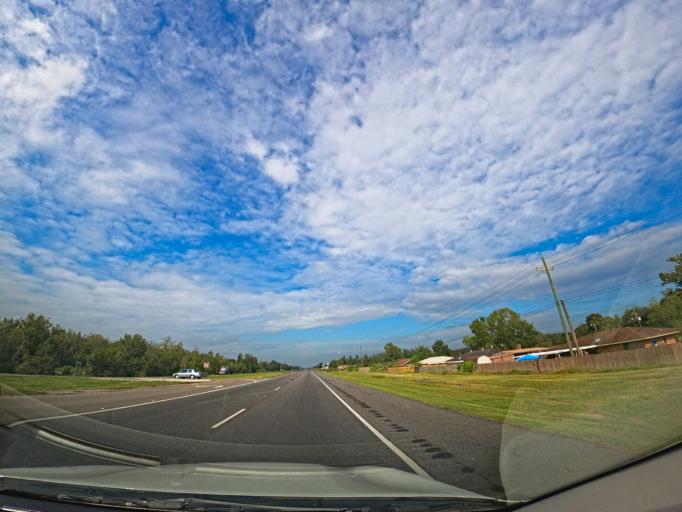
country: US
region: Louisiana
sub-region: Saint Mary Parish
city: Patterson
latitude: 29.6921
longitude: -91.3250
